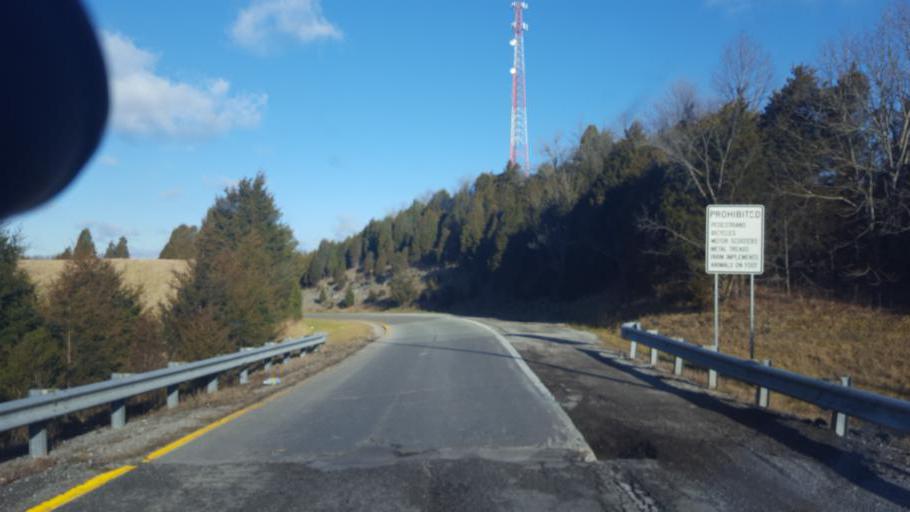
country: US
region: Kentucky
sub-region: Scott County
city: Georgetown
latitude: 38.3800
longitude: -84.5695
